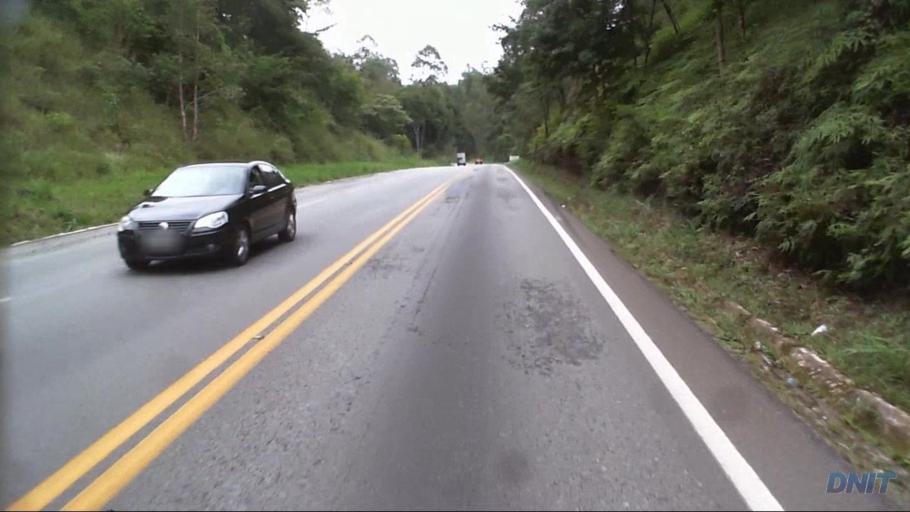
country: BR
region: Minas Gerais
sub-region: Joao Monlevade
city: Joao Monlevade
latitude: -19.8443
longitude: -43.1056
